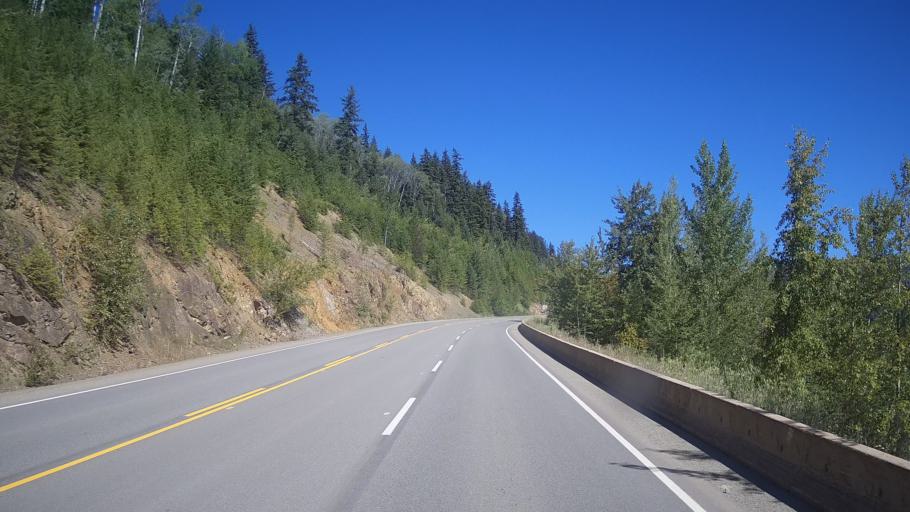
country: CA
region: British Columbia
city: Kamloops
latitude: 51.4844
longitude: -120.2644
